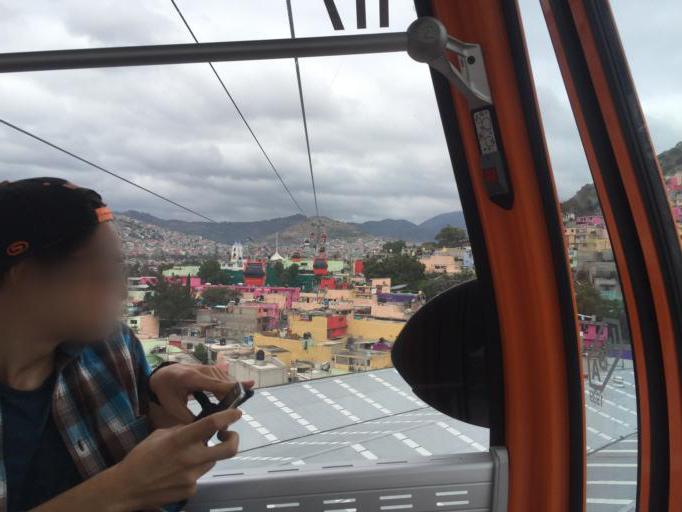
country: MX
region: Mexico
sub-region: Tlalnepantla de Baz
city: Puerto Escondido (Tepeolulco Puerto Escondido)
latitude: 19.5413
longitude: -99.0606
